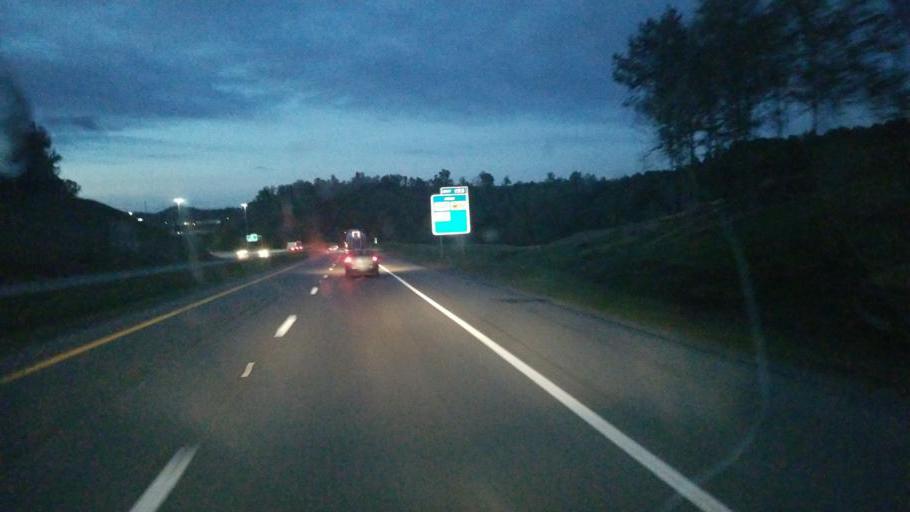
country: US
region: West Virginia
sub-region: Monongalia County
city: Star City
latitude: 39.6468
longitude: -80.0069
